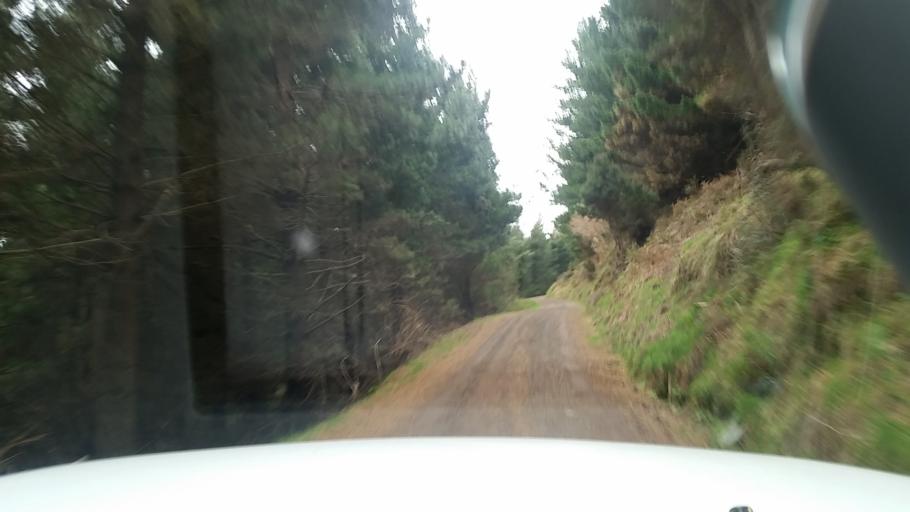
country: NZ
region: Canterbury
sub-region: Christchurch City
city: Christchurch
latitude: -43.7083
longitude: 172.7780
